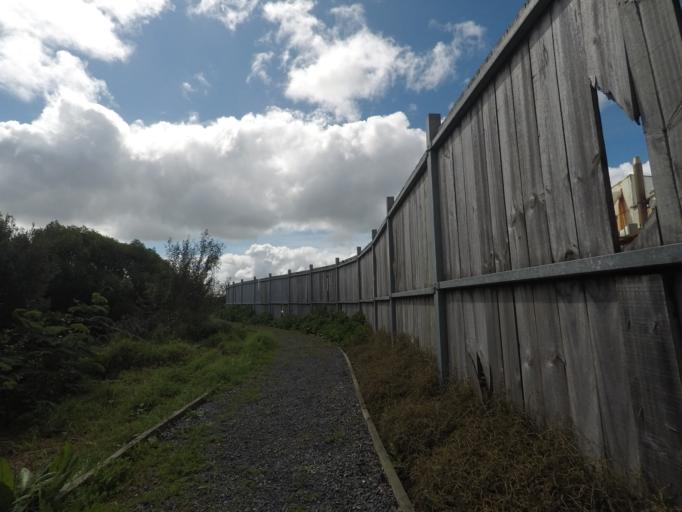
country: NZ
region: Auckland
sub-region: Auckland
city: Rosebank
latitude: -36.8778
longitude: 174.6654
